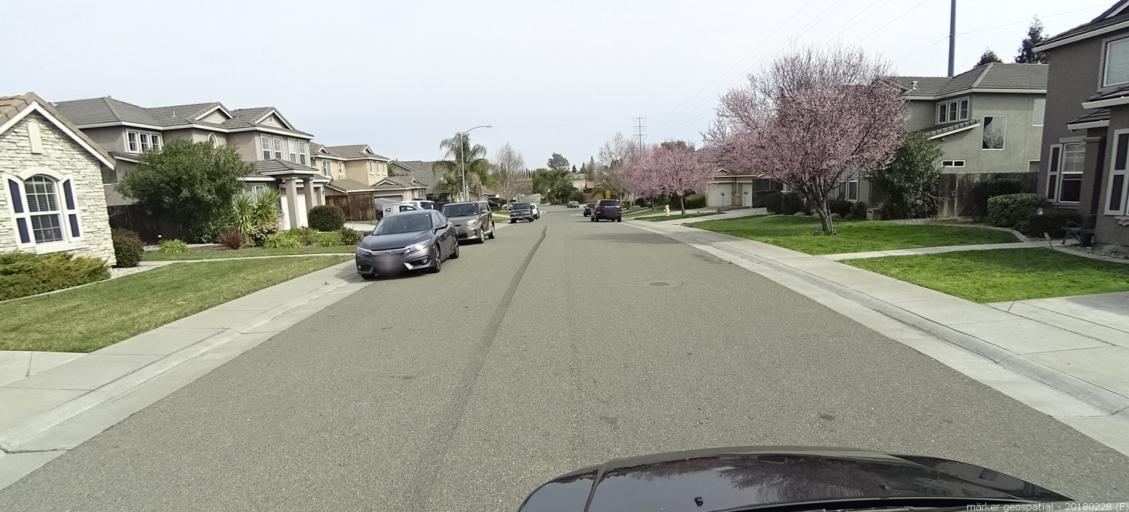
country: US
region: California
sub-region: Sacramento County
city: Antelope
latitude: 38.7074
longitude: -121.3437
